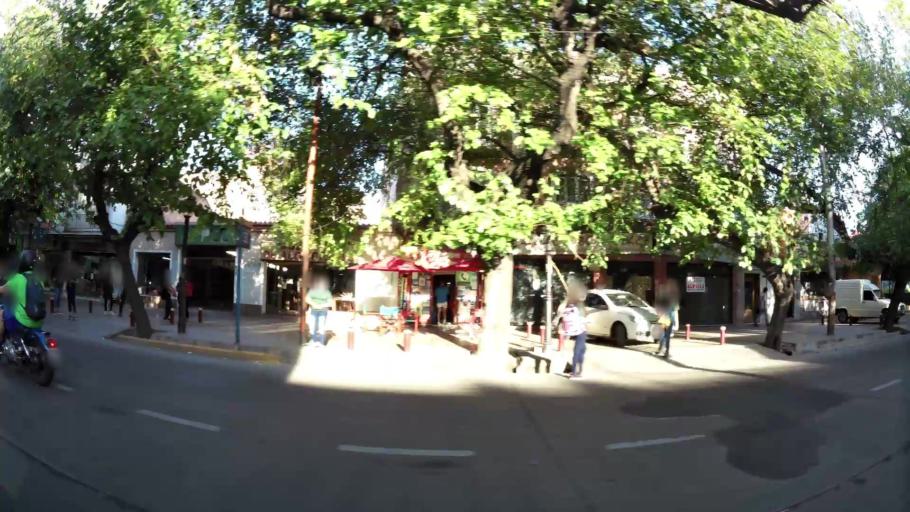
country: AR
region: Mendoza
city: Mendoza
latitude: -32.8960
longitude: -68.8380
